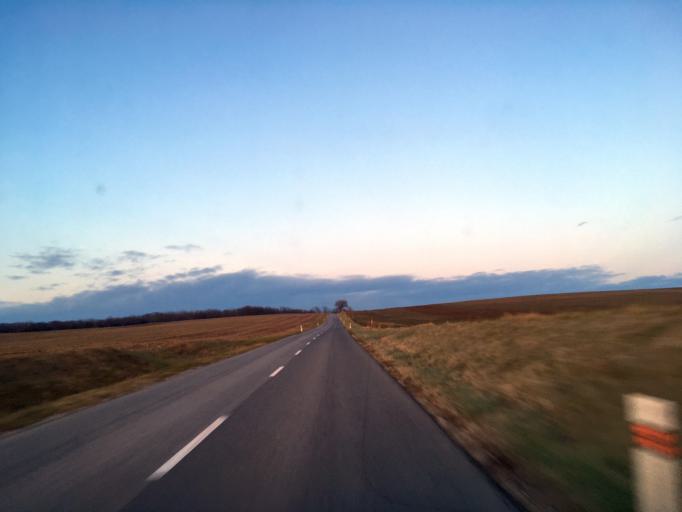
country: SK
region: Nitriansky
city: Svodin
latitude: 47.8558
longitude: 18.4487
